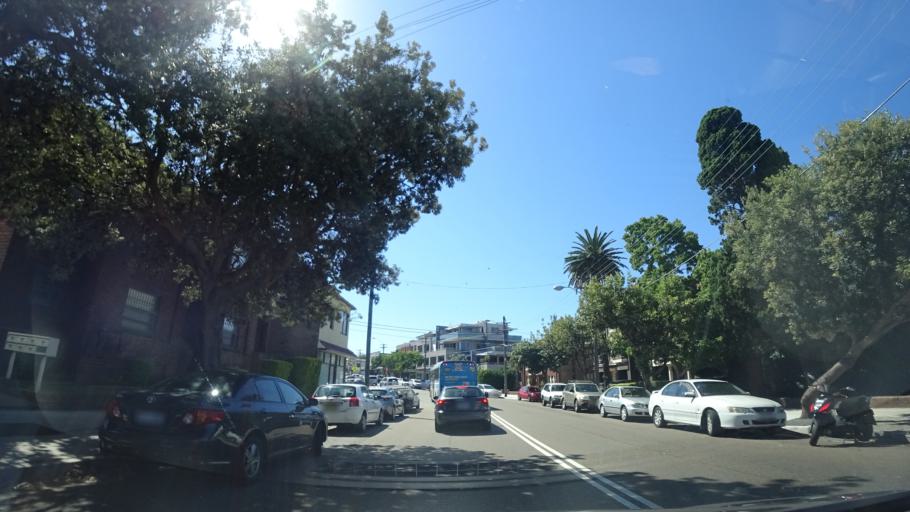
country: AU
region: New South Wales
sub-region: Randwick
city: Randwick
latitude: -33.9111
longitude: 151.2528
